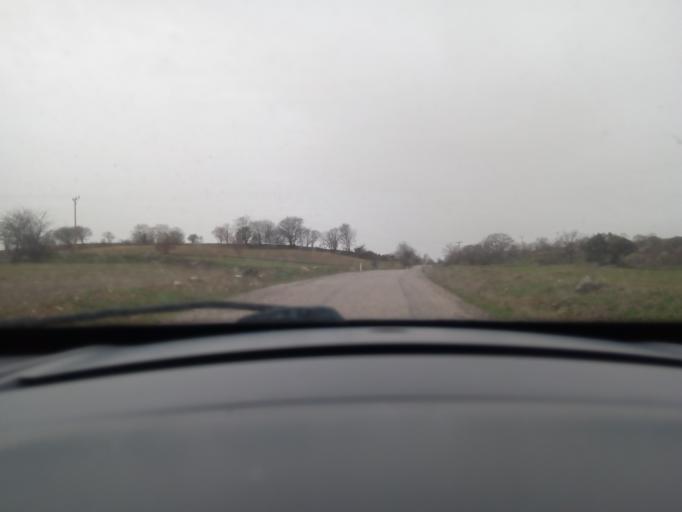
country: TR
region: Balikesir
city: Susurluk
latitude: 39.9207
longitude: 28.0715
